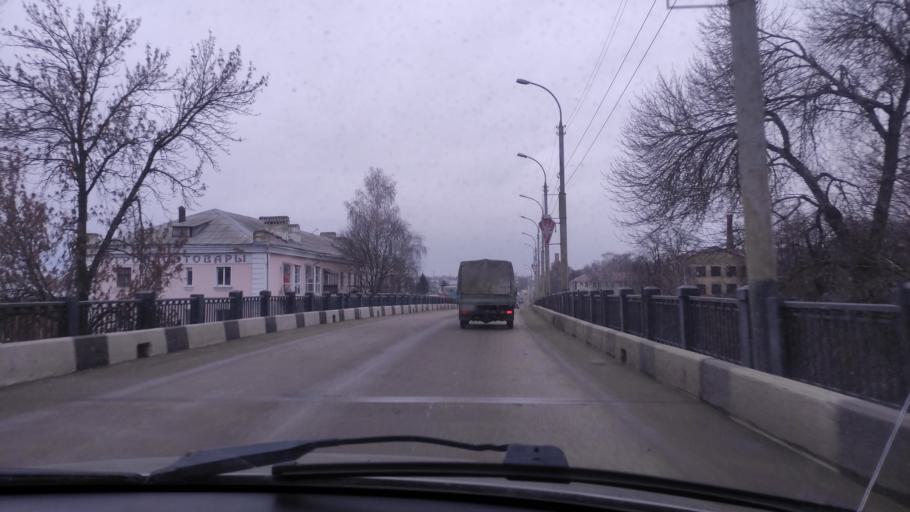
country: RU
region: Tambov
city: Tambov
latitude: 52.7219
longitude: 41.4222
